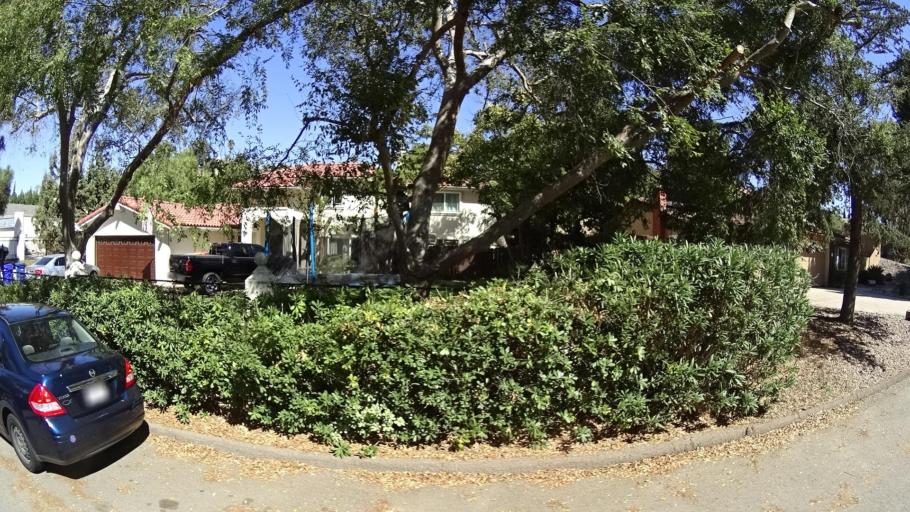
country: US
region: California
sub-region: San Diego County
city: Bonita
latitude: 32.6599
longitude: -117.0174
